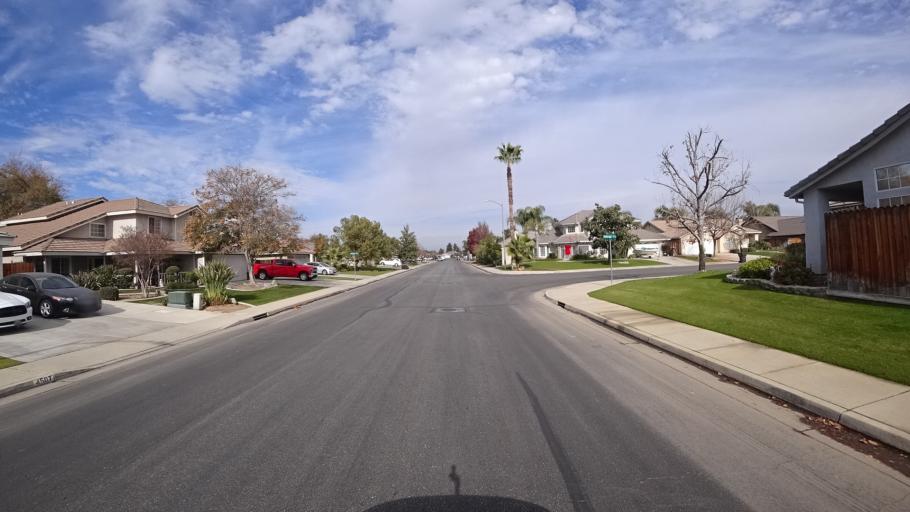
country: US
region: California
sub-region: Kern County
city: Greenacres
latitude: 35.4017
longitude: -119.1271
